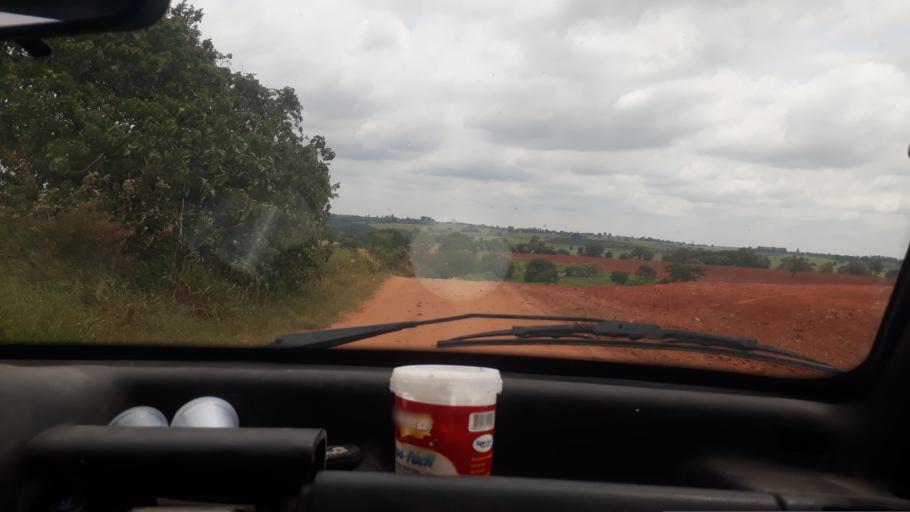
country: BR
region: Sao Paulo
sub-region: Regente Feijo
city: Regente Feijo
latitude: -22.2538
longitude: -51.2998
